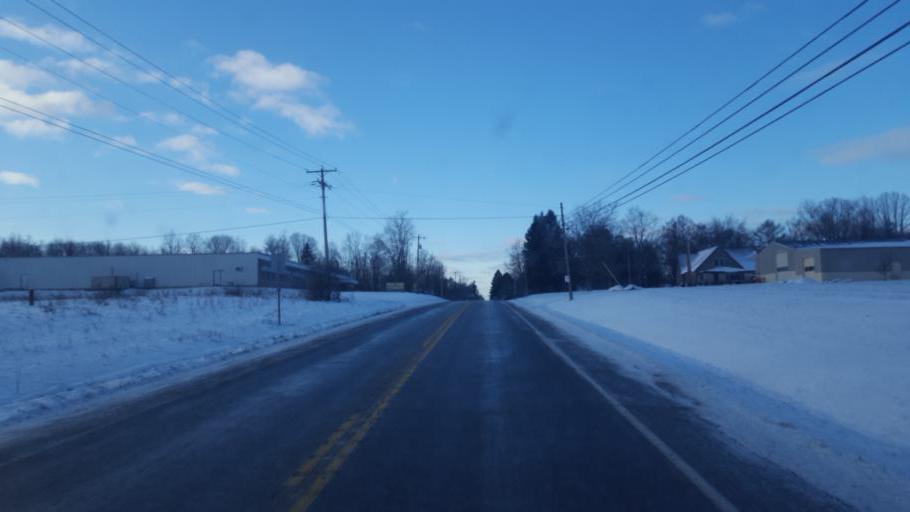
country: US
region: Pennsylvania
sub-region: Mercer County
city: Stoneboro
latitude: 41.3892
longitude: -80.2166
